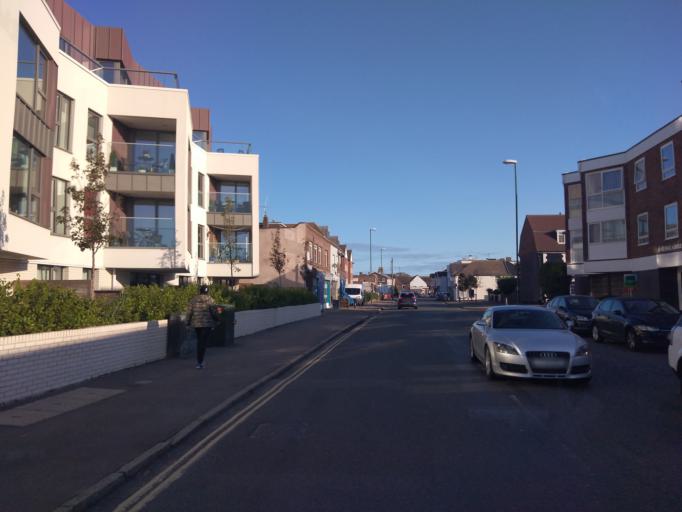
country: GB
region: England
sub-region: West Sussex
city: Lancing
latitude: 50.8215
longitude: -0.3246
